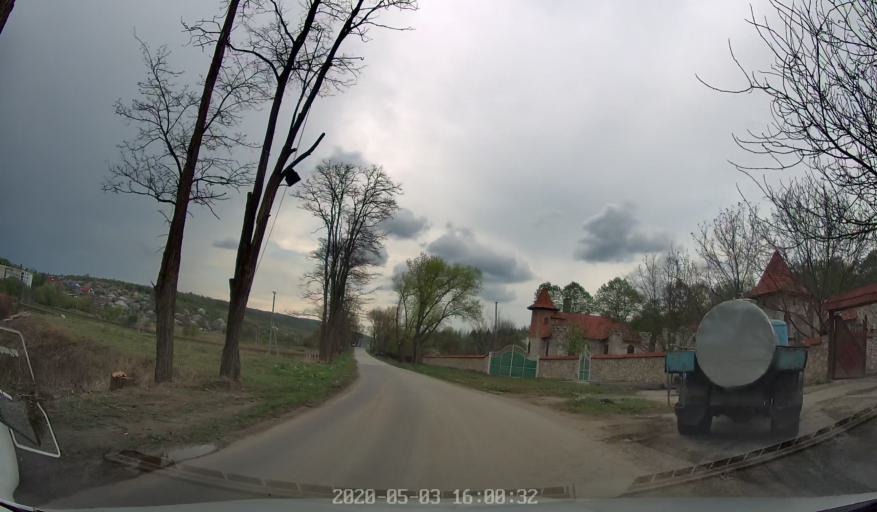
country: MD
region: Stinga Nistrului
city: Bucovat
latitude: 47.1609
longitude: 28.4190
